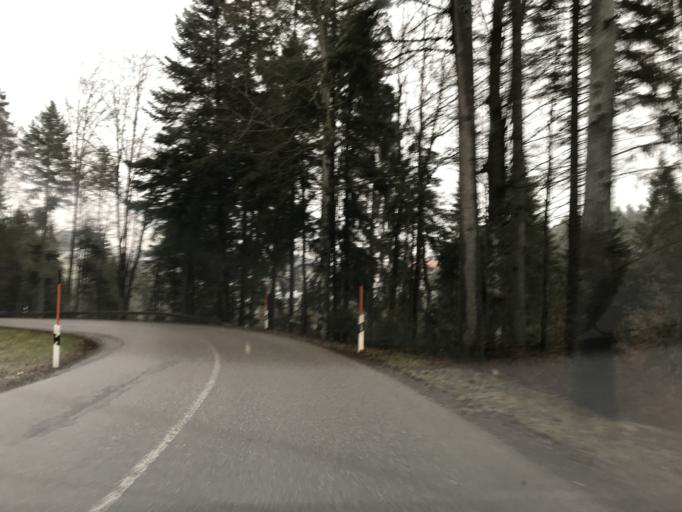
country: DE
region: Baden-Wuerttemberg
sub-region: Freiburg Region
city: Rickenbach
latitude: 47.6137
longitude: 7.9763
